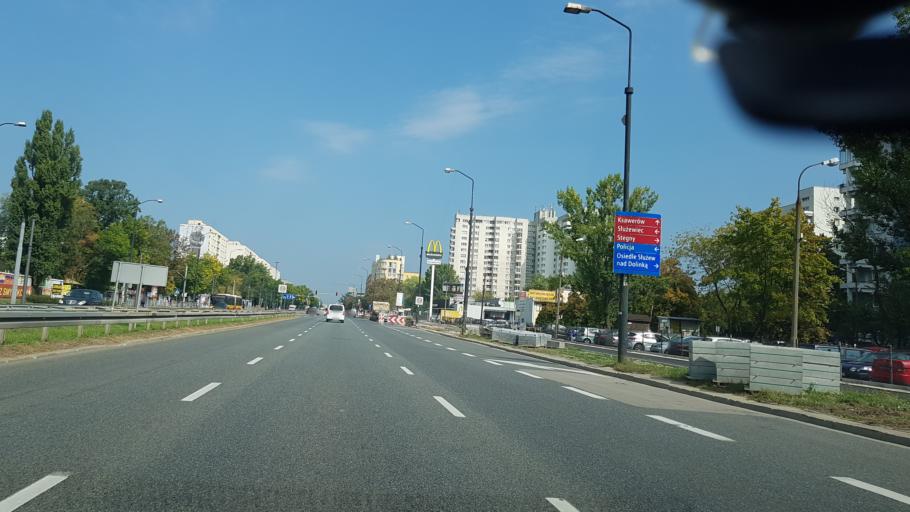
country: PL
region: Masovian Voivodeship
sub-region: Warszawa
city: Mokotow
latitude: 52.1712
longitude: 21.0193
